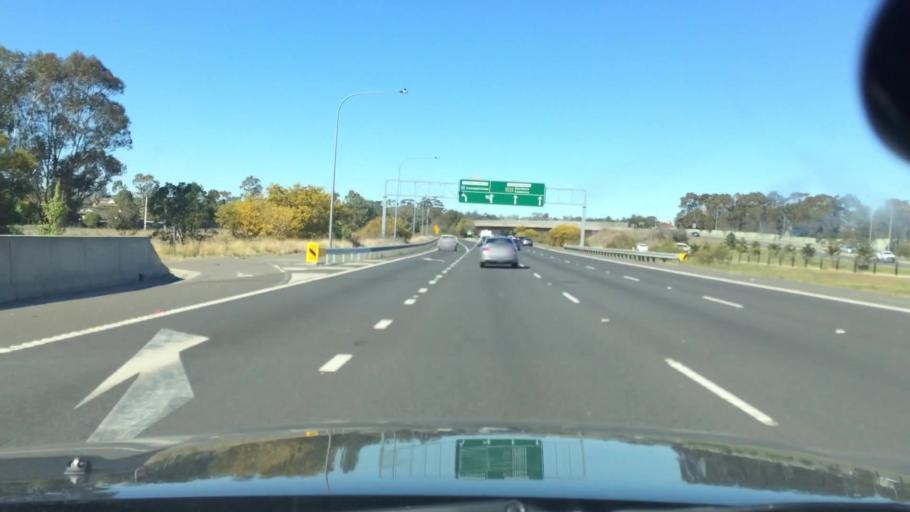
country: AU
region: New South Wales
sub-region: Campbelltown Municipality
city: Leumeah
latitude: -34.0299
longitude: 150.8242
